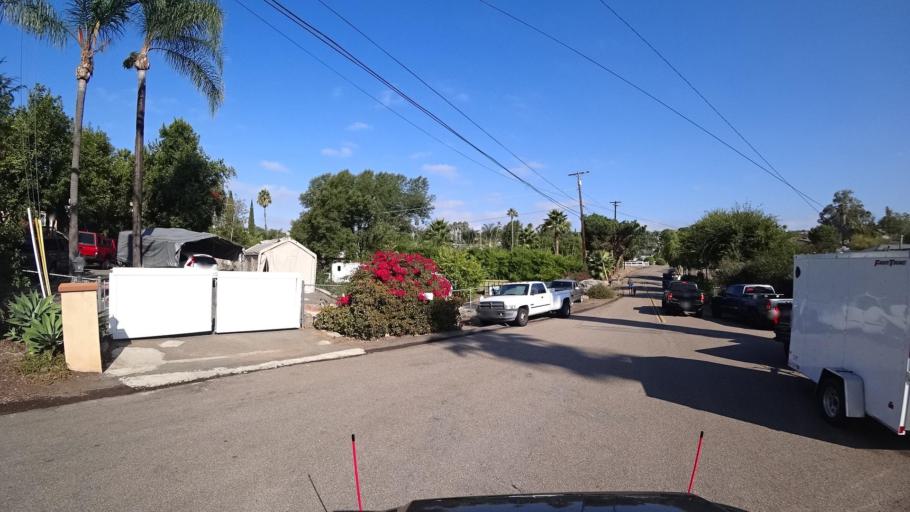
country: US
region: California
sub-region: San Diego County
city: Vista
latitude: 33.1743
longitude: -117.2244
